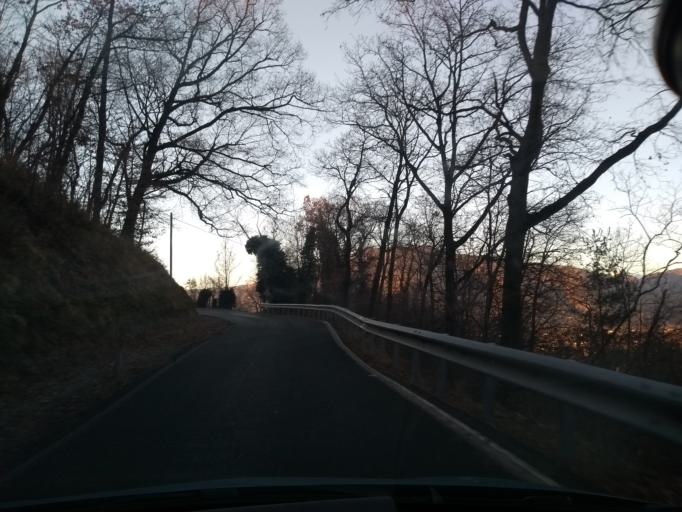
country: IT
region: Piedmont
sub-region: Provincia di Torino
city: Balangero
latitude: 45.2745
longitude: 7.5277
